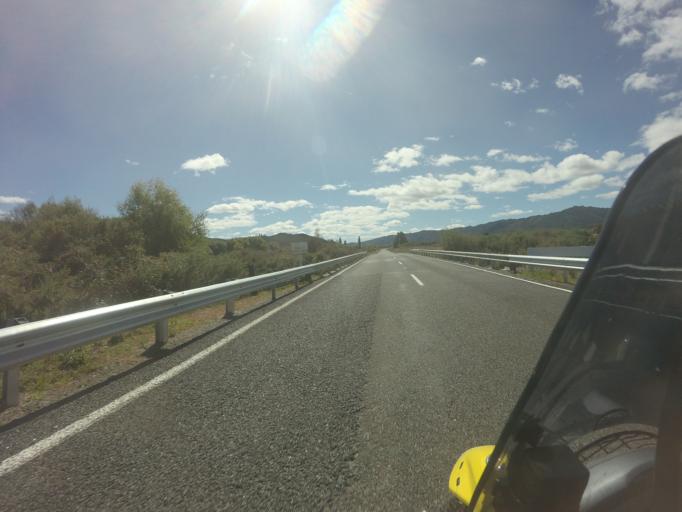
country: NZ
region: Bay of Plenty
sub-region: Kawerau District
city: Kawerau
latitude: -38.2460
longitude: 176.8261
